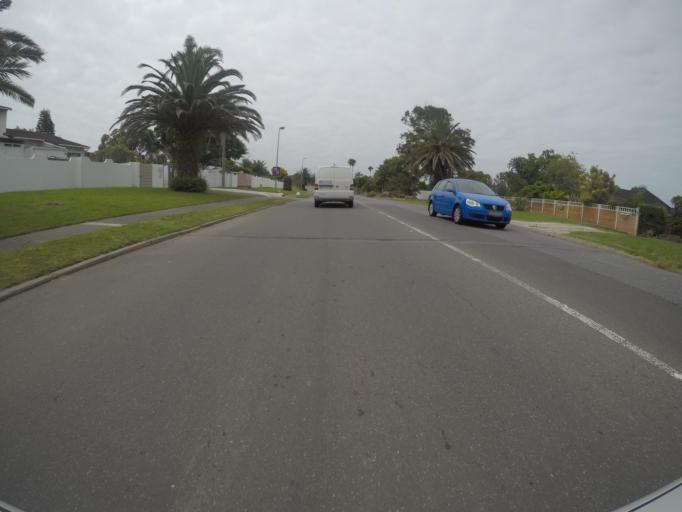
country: ZA
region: Eastern Cape
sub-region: Buffalo City Metropolitan Municipality
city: East London
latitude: -32.9752
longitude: 27.9410
